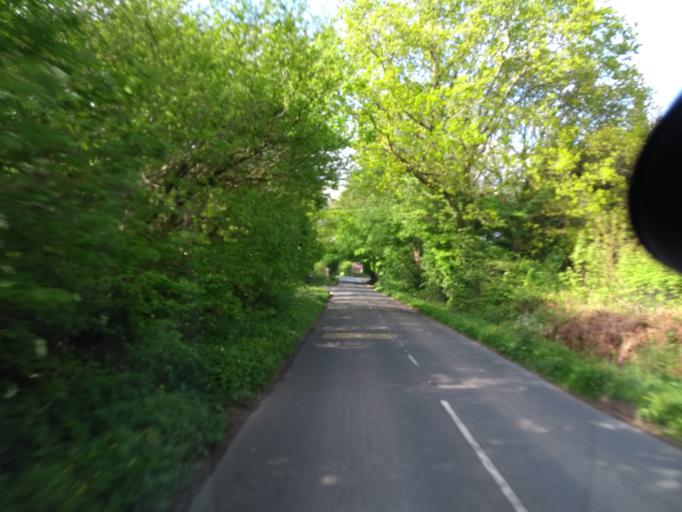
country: GB
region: England
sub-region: Dorset
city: Lyme Regis
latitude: 50.7689
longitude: -2.9531
